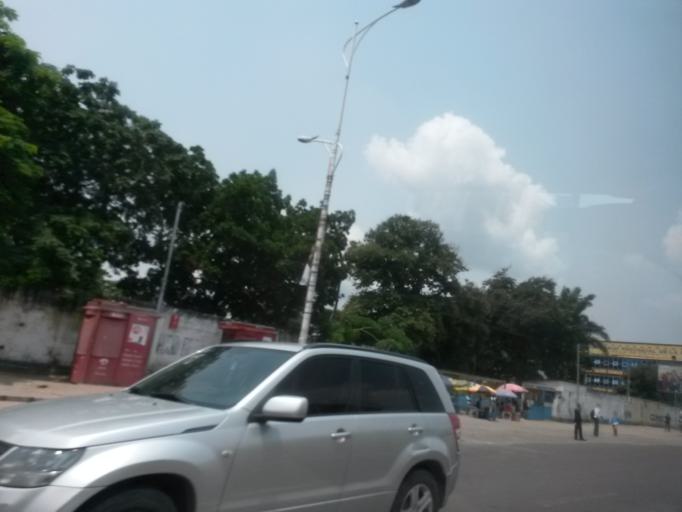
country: CD
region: Kinshasa
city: Kinshasa
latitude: -4.3148
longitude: 15.2910
